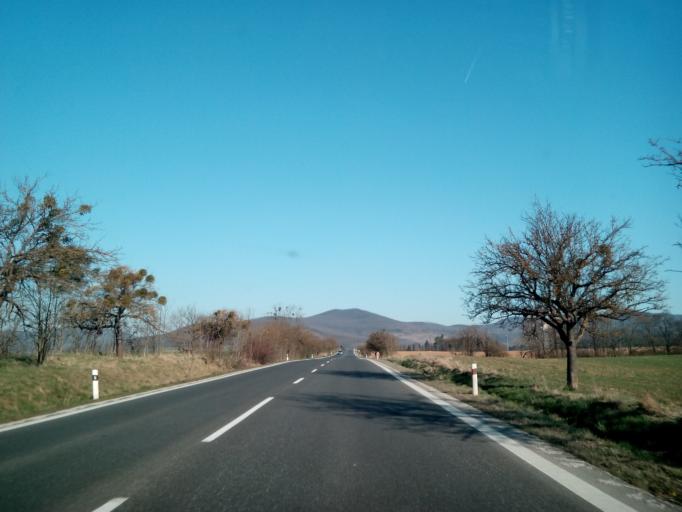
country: SK
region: Kosicky
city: Roznava
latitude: 48.6376
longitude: 20.6129
